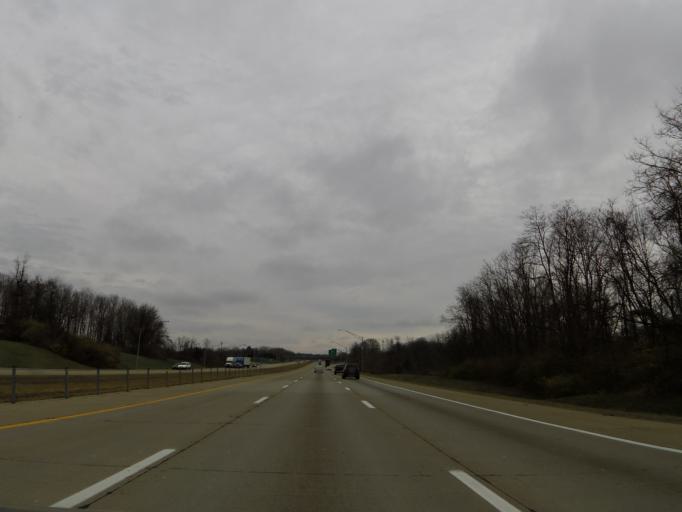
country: US
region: Kentucky
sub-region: Boone County
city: Hebron
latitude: 39.0724
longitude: -84.6637
